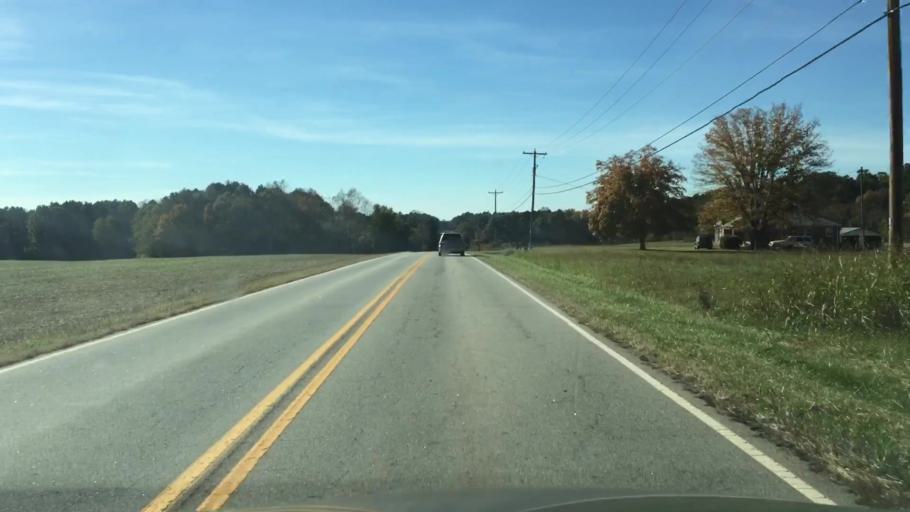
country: US
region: North Carolina
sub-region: Rowan County
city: China Grove
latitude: 35.6486
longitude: -80.6176
